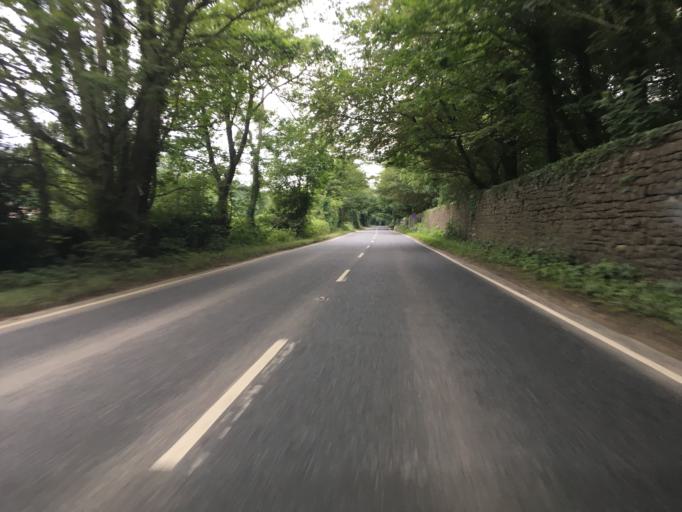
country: GB
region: England
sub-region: North Somerset
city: Long Ashton
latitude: 51.4486
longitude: -2.6577
